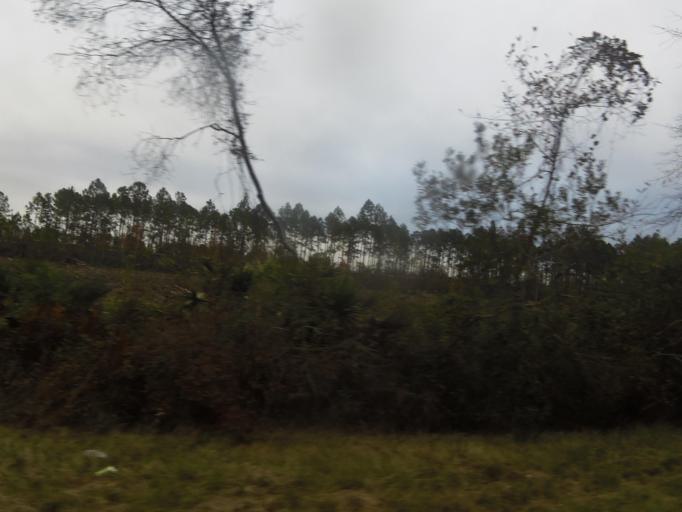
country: US
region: Georgia
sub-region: Charlton County
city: Folkston
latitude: 30.8657
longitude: -82.0387
